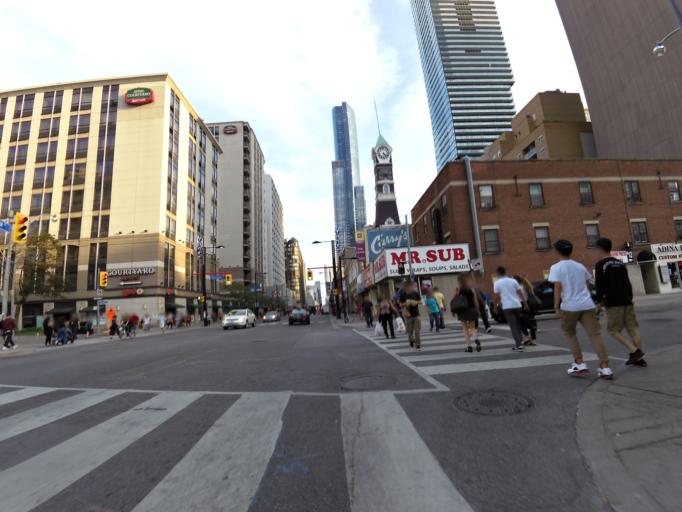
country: CA
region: Ontario
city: Toronto
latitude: 43.6631
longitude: -79.3839
